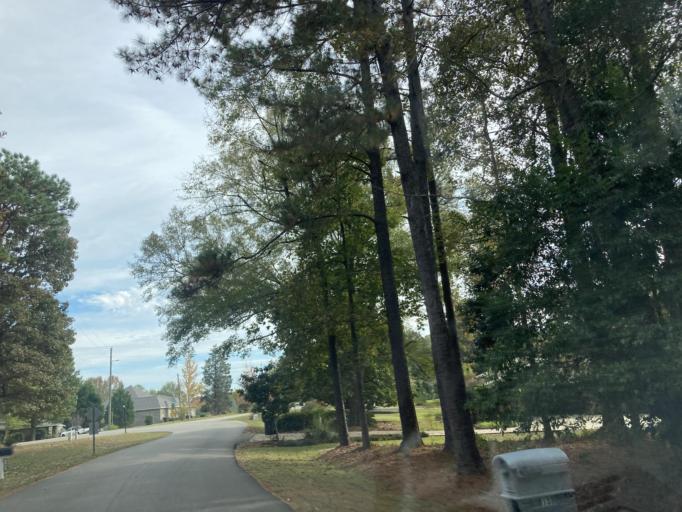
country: US
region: Mississippi
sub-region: Lamar County
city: West Hattiesburg
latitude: 31.3244
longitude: -89.4310
